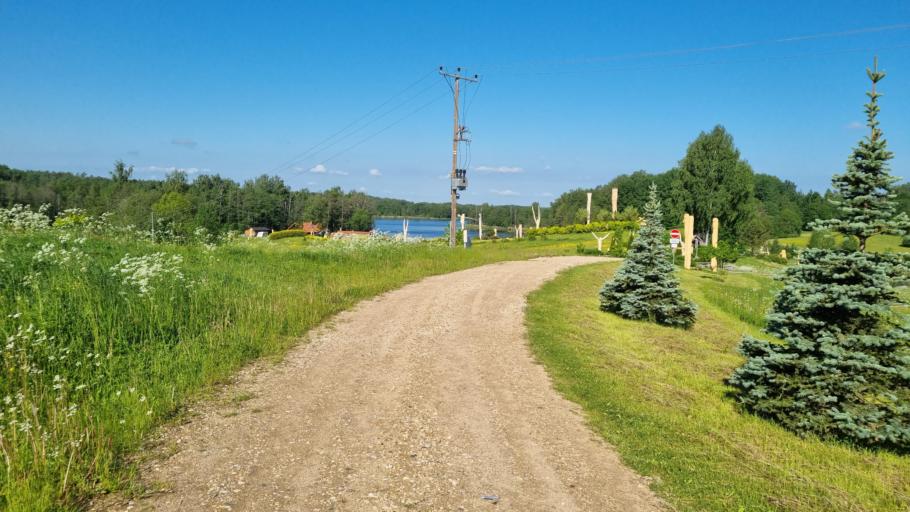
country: LV
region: Aglona
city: Aglona
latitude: 56.1243
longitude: 27.0402
